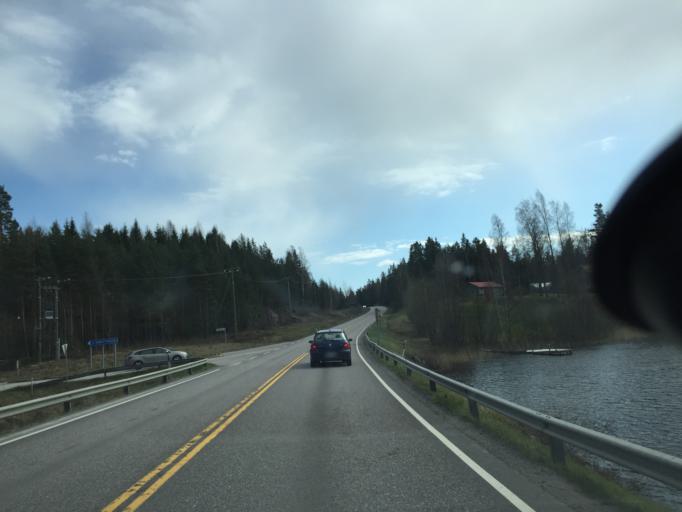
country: FI
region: Uusimaa
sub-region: Raaseporin
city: Ekenaes
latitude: 60.0329
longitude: 23.3680
